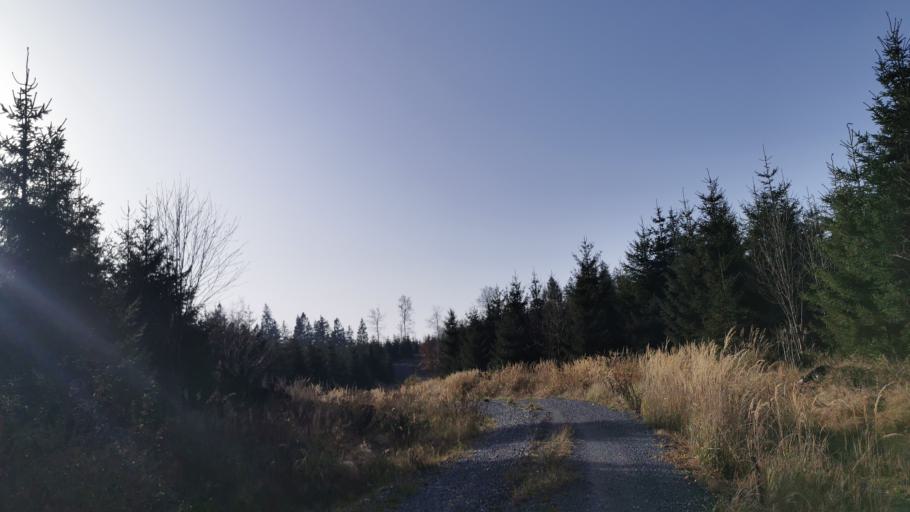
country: DE
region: Bavaria
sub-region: Upper Franconia
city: Tschirn
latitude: 50.4388
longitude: 11.4608
